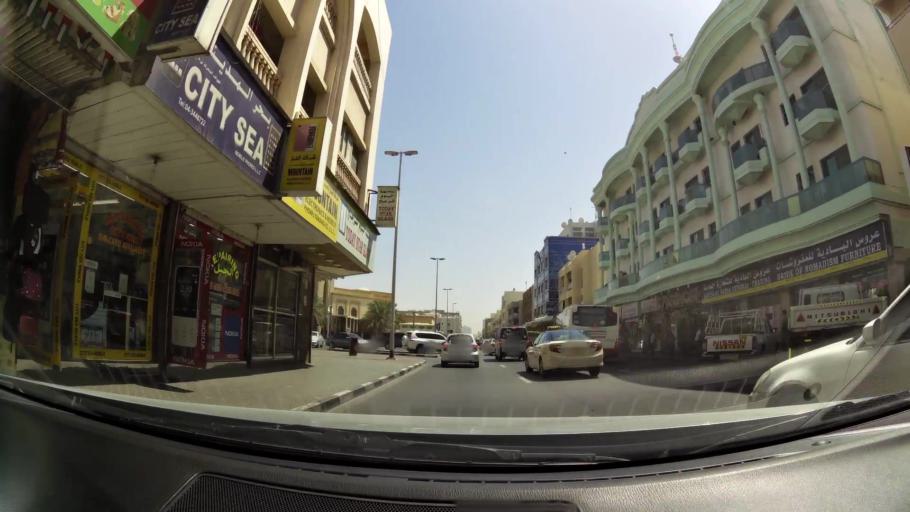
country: AE
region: Ash Shariqah
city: Sharjah
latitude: 25.2310
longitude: 55.2769
